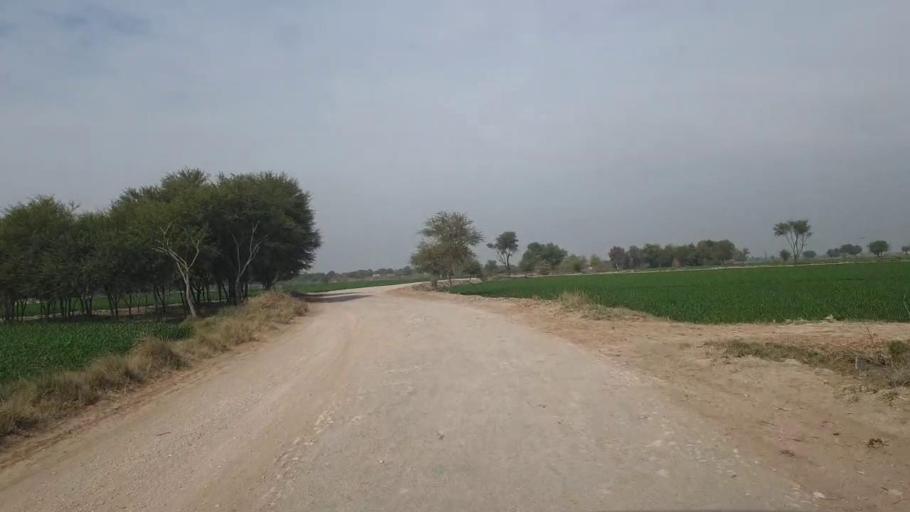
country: PK
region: Sindh
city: Nawabshah
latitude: 26.1125
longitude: 68.4804
